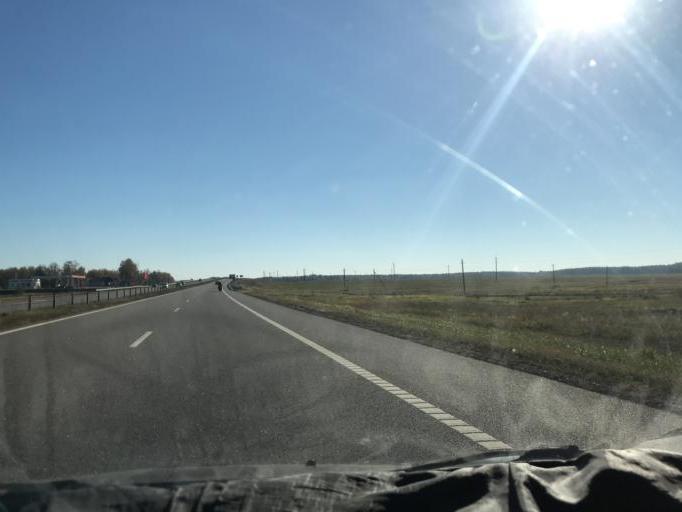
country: BY
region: Mogilev
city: Yalizava
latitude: 53.2193
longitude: 29.0269
